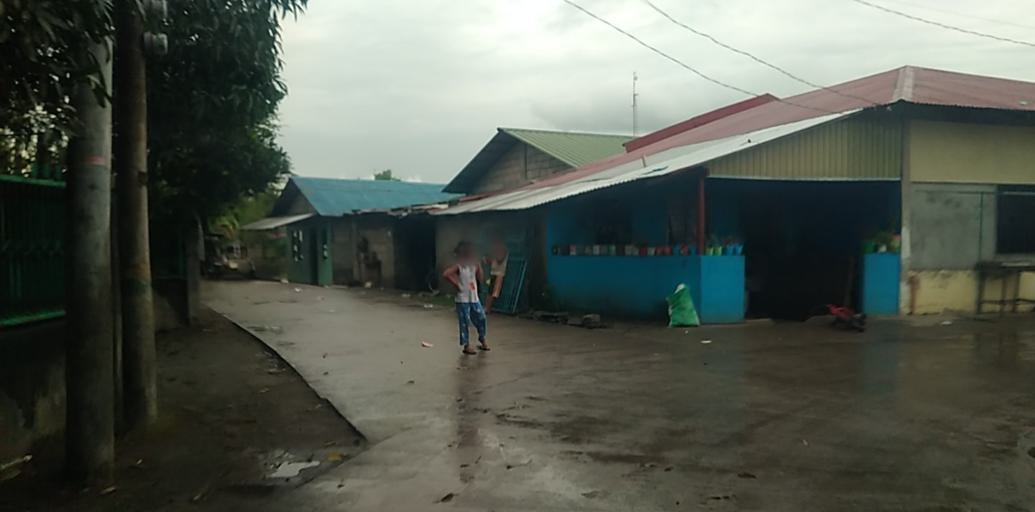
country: PH
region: Central Luzon
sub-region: Province of Pampanga
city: Anao
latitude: 15.1465
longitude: 120.7239
